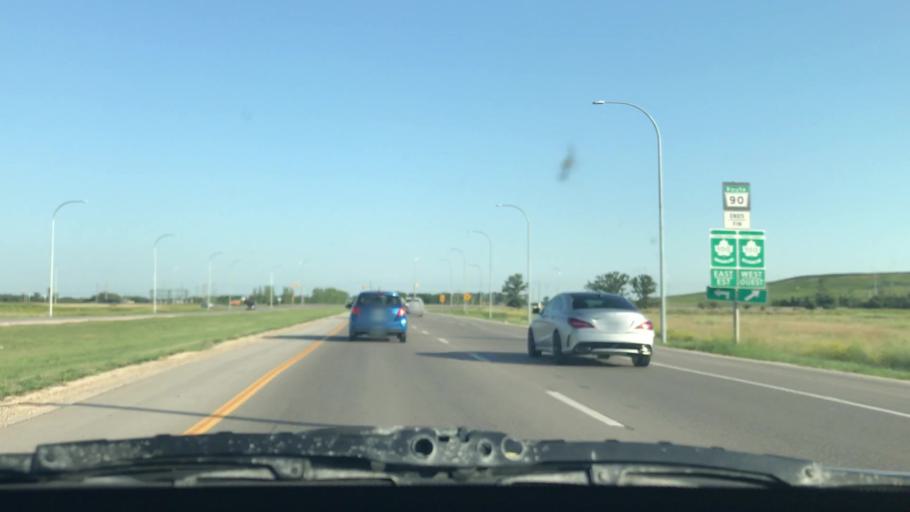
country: CA
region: Manitoba
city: Winnipeg
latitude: 49.7713
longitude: -97.1843
